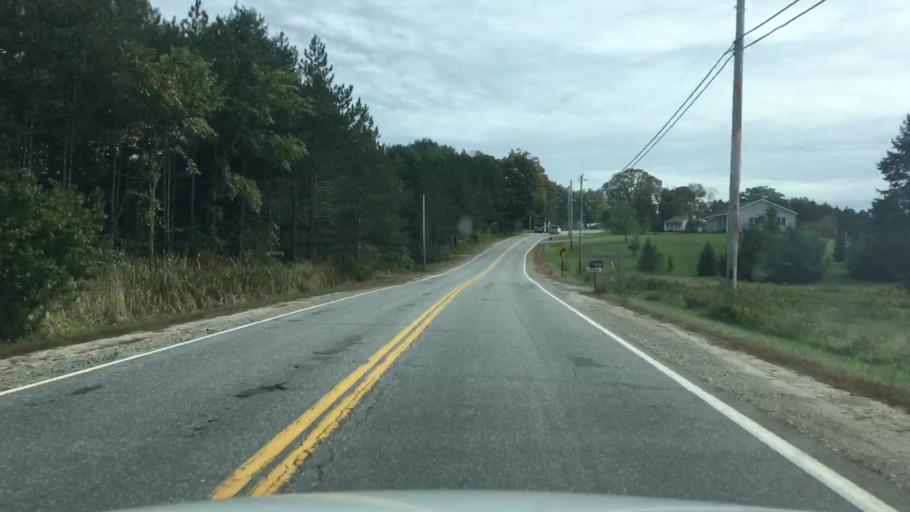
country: US
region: Maine
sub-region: Androscoggin County
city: Lisbon Falls
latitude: 43.9523
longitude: -70.0338
